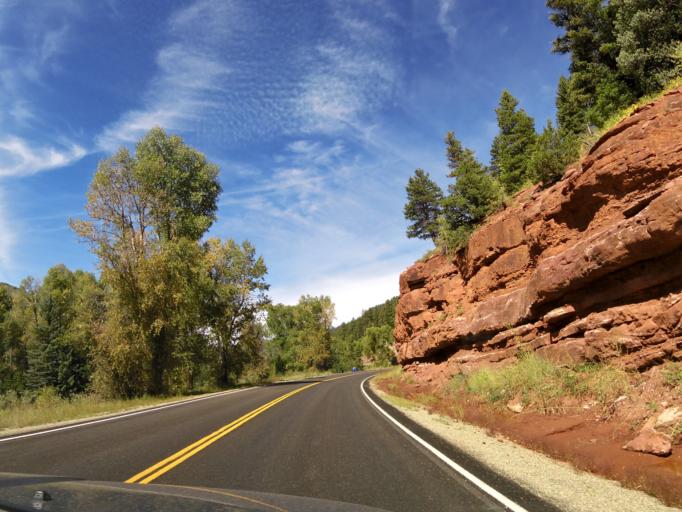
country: US
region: Colorado
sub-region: Montezuma County
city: Mancos
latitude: 37.5756
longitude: -108.1867
